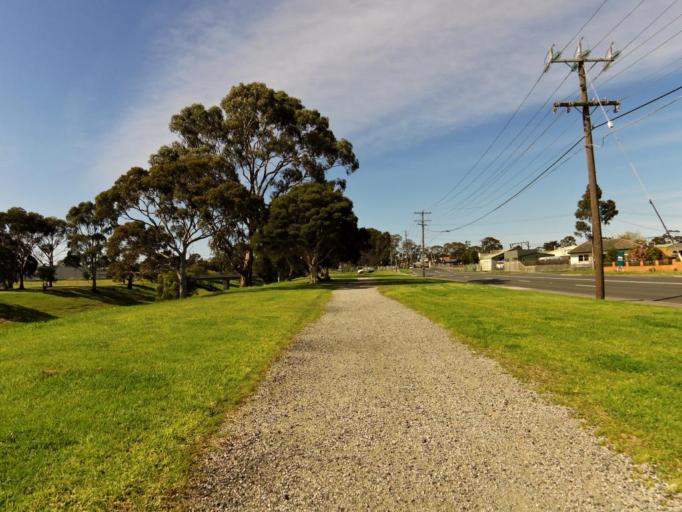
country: AU
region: Victoria
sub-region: Greater Dandenong
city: Dandenong
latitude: -37.9935
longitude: 145.2125
